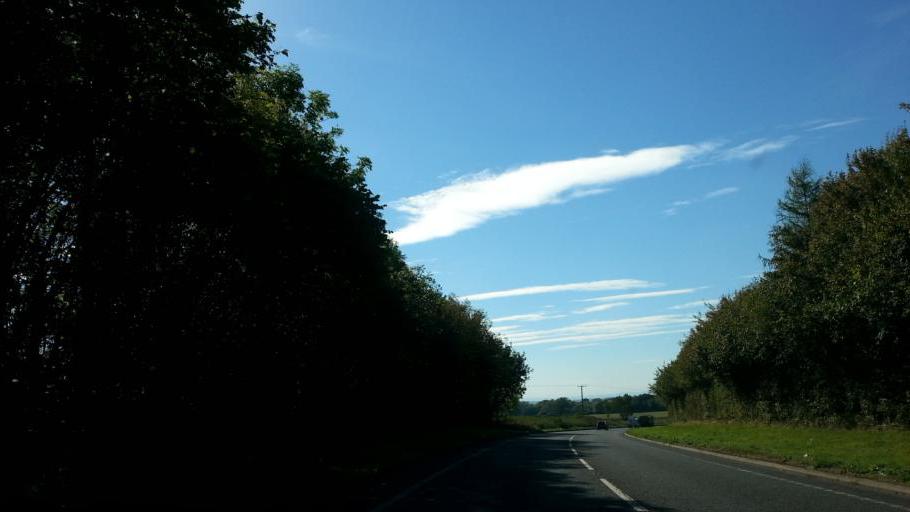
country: GB
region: England
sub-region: Telford and Wrekin
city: Newport
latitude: 52.7543
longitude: -2.3761
